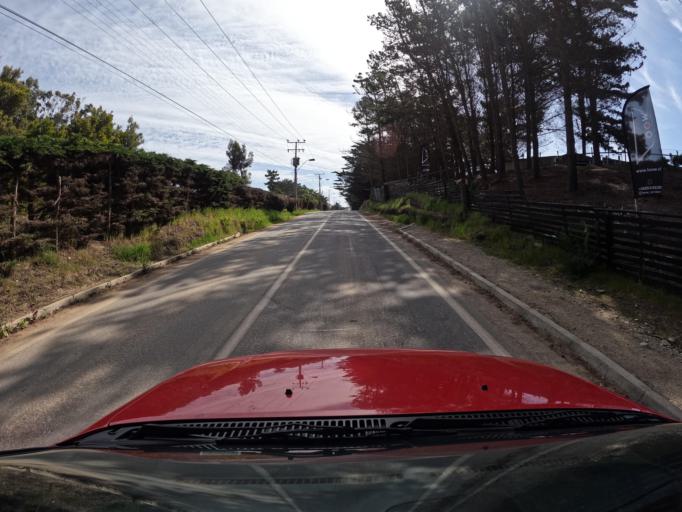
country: CL
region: O'Higgins
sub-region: Provincia de Colchagua
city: Santa Cruz
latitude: -34.4298
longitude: -72.0356
